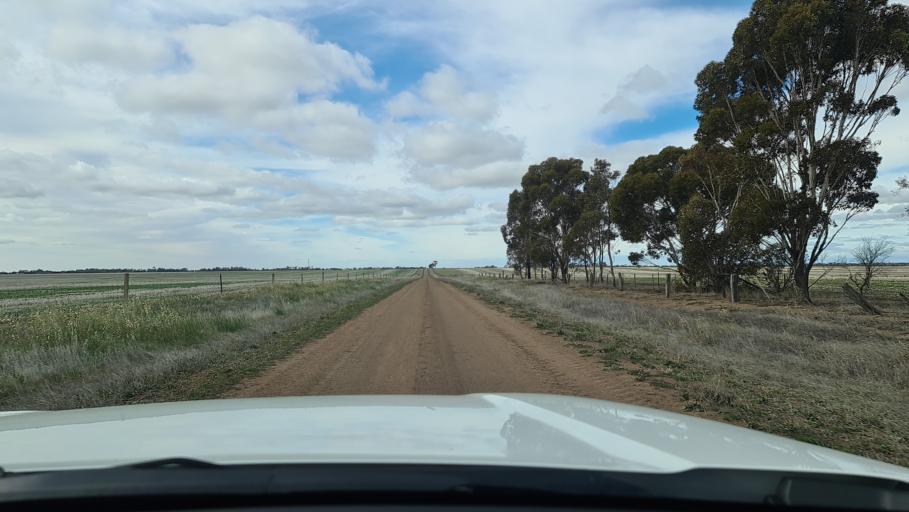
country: AU
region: Victoria
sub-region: Horsham
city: Horsham
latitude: -36.6313
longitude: 142.4297
